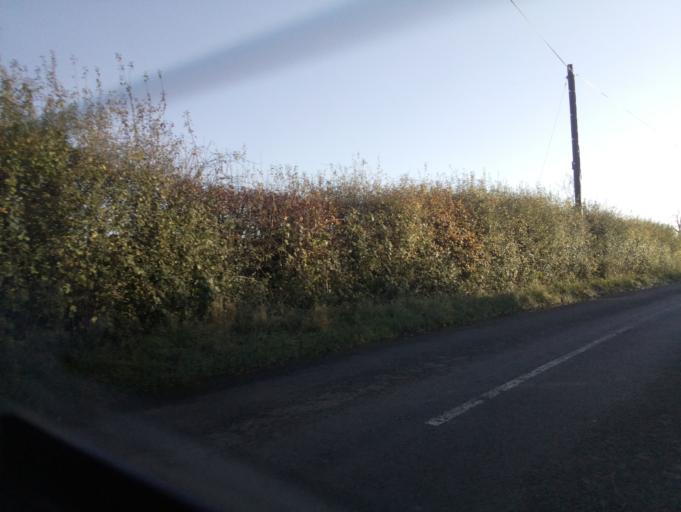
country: GB
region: England
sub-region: Somerset
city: Milborne Port
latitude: 50.9826
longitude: -2.4633
